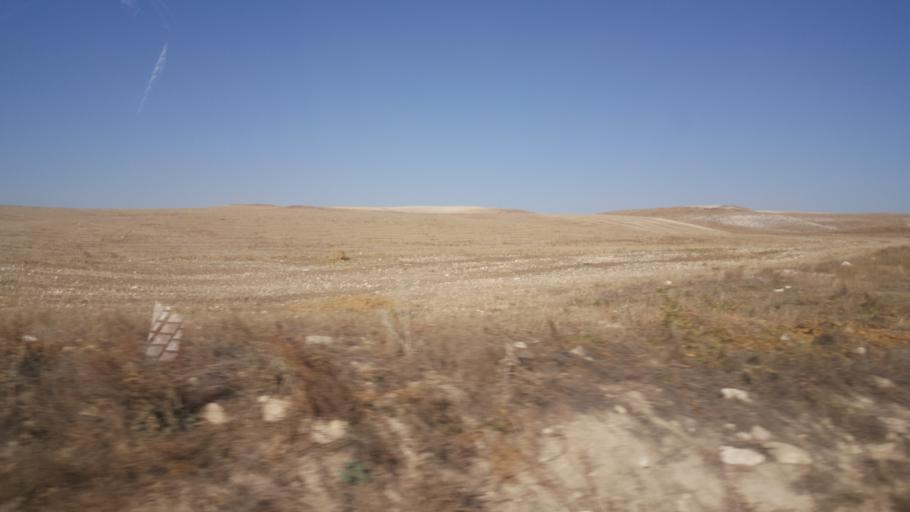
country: TR
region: Konya
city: Celtik
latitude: 39.0909
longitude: 32.0631
